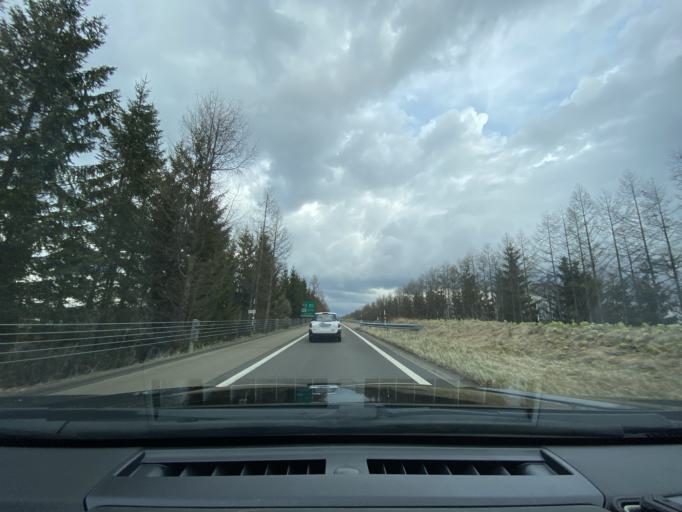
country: JP
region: Hokkaido
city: Otofuke
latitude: 42.9798
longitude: 143.1636
